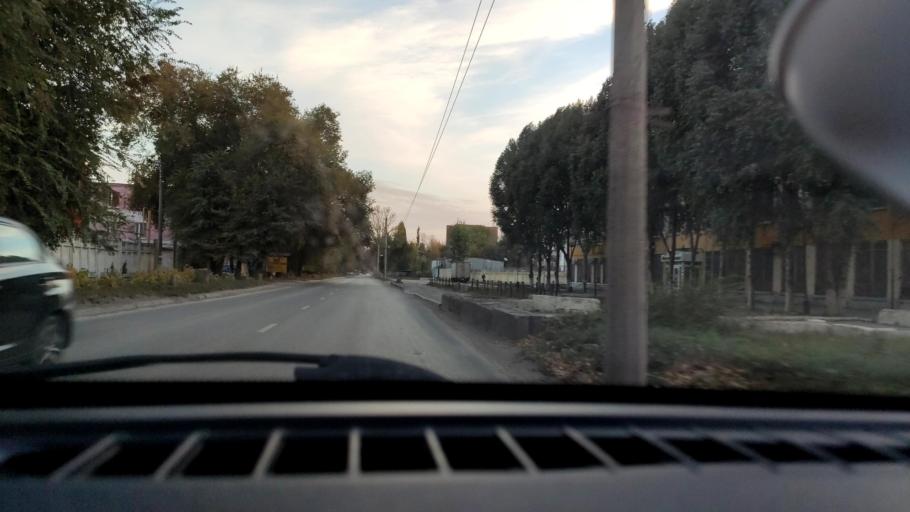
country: RU
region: Samara
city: Samara
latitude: 53.1928
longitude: 50.2455
